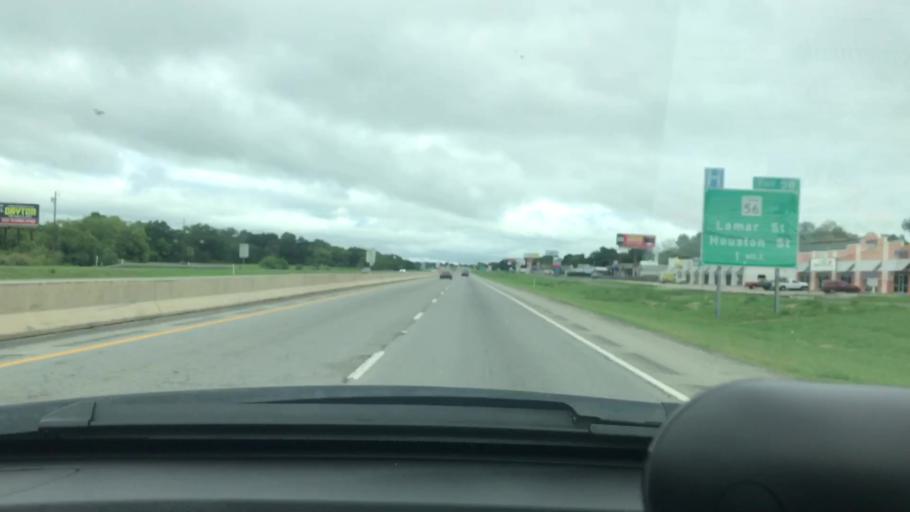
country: US
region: Texas
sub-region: Grayson County
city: Sherman
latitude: 33.6190
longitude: -96.6106
